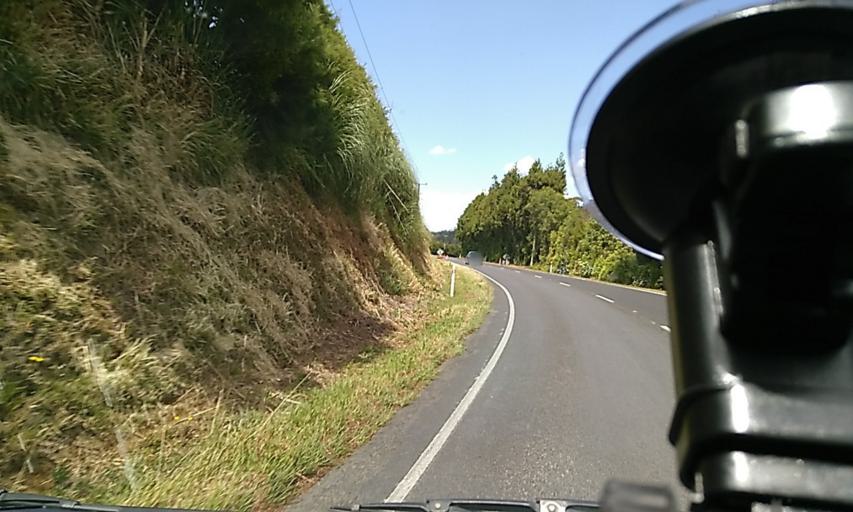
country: NZ
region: Bay of Plenty
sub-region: Western Bay of Plenty District
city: Waihi Beach
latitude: -37.4533
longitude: 175.9424
